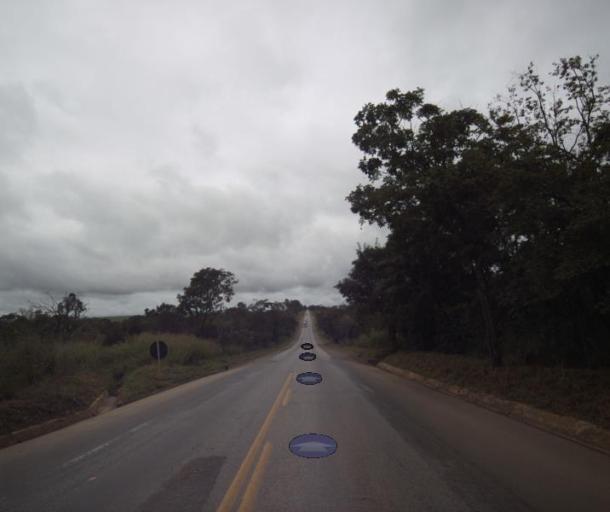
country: BR
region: Goias
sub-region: Uruacu
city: Uruacu
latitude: -14.6119
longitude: -49.1686
